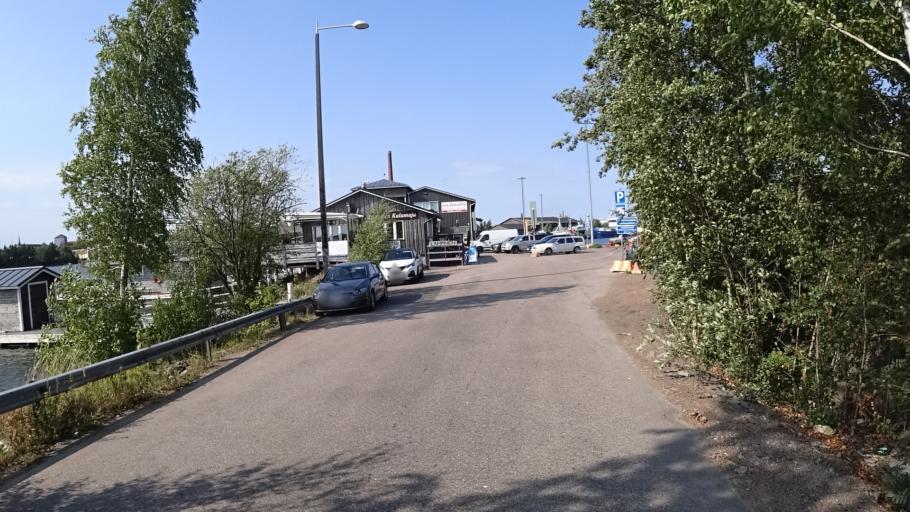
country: FI
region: Kymenlaakso
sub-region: Kotka-Hamina
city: Kotka
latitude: 60.4595
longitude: 26.9637
